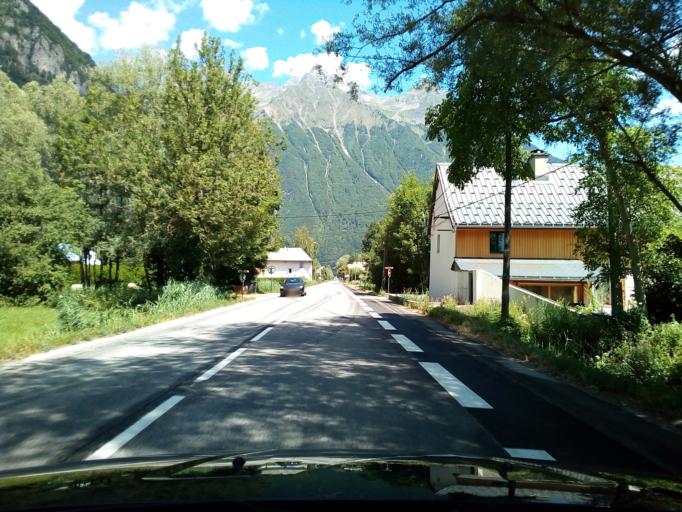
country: FR
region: Rhone-Alpes
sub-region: Departement de l'Isere
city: Huez
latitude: 45.1025
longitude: 6.0086
